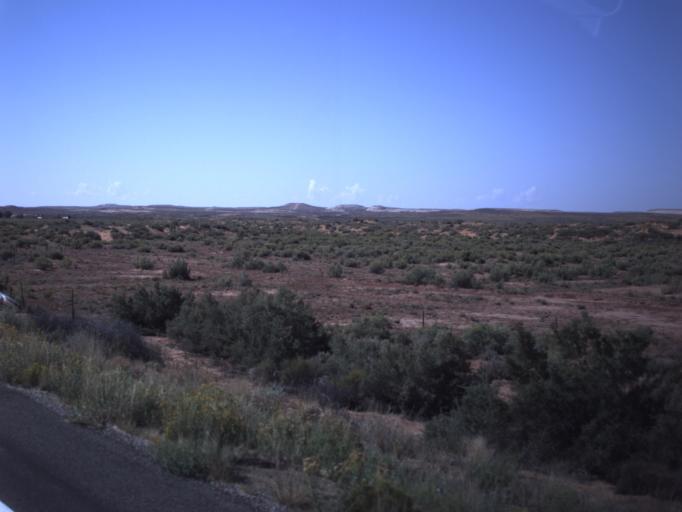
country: US
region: Utah
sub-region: San Juan County
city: Blanding
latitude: 37.1188
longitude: -109.5450
